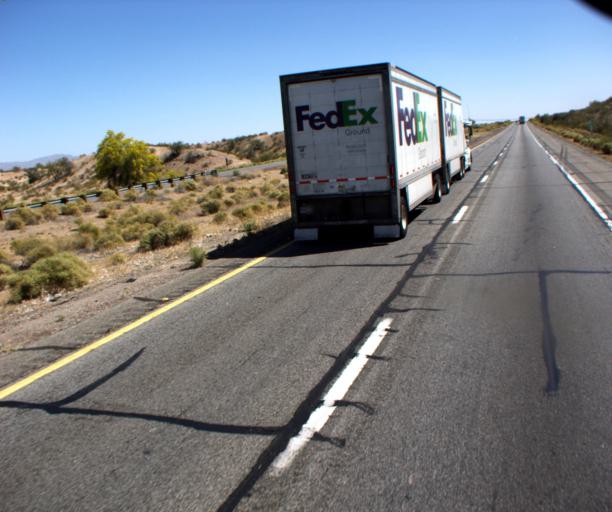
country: US
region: Arizona
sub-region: Maricopa County
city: Buckeye
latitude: 33.4569
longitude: -112.7567
